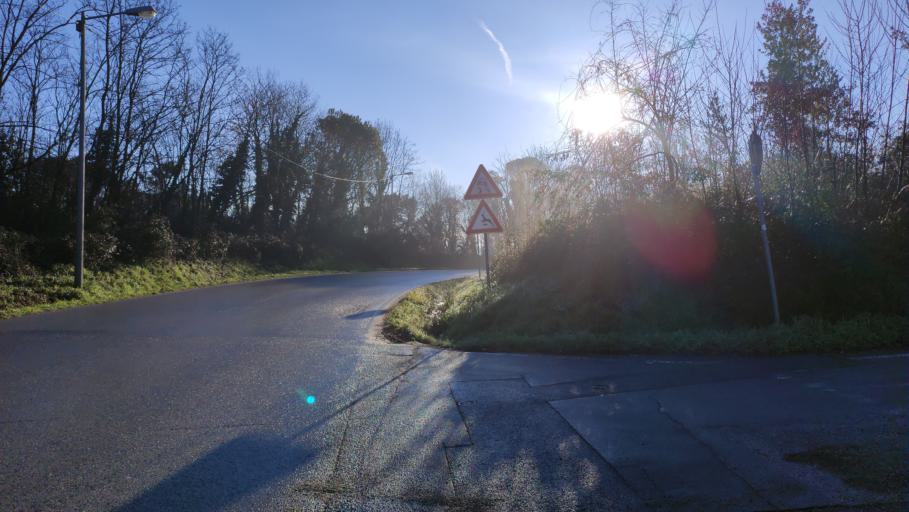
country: IT
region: Tuscany
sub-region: Provincia di Pistoia
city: Cantagrillo-Casalguidi
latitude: 43.8693
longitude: 10.9344
